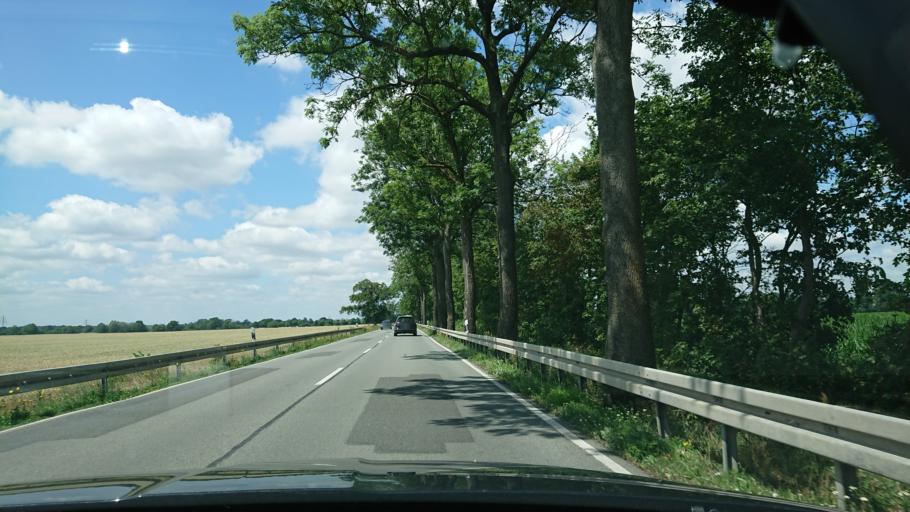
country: DE
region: Brandenburg
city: Perleberg
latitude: 53.0517
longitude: 11.9220
